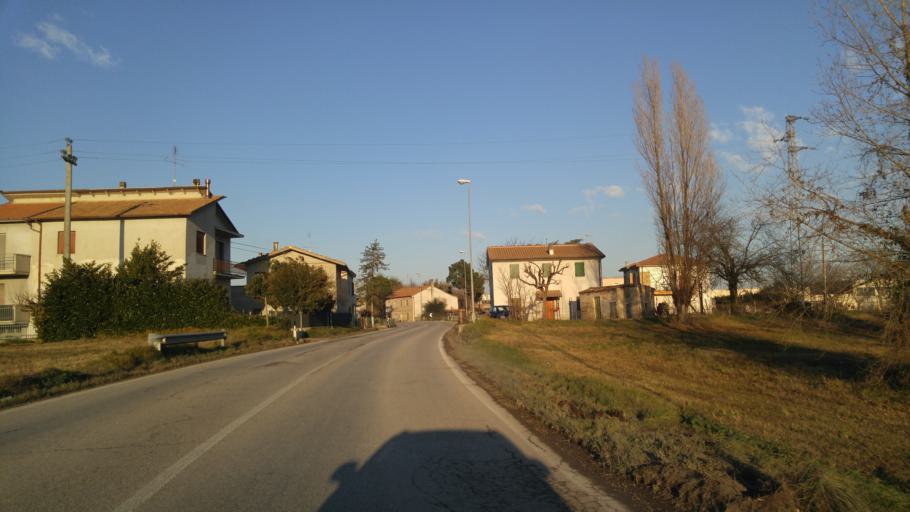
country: IT
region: The Marches
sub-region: Provincia di Pesaro e Urbino
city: San Michele
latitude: 43.6623
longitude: 12.9989
